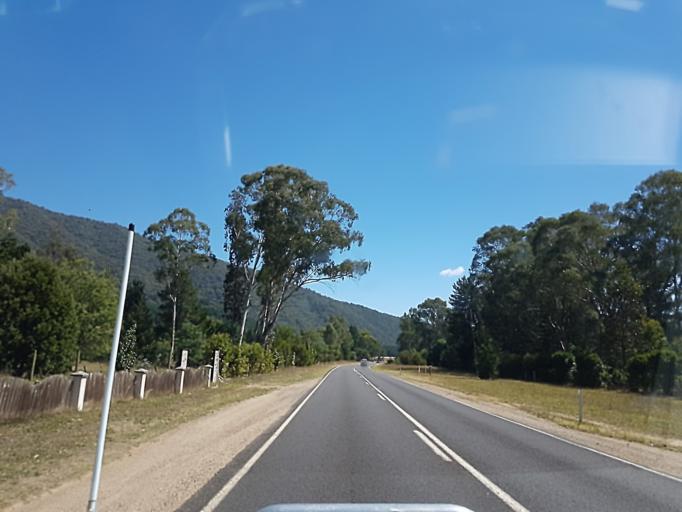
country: AU
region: Victoria
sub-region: Alpine
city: Mount Beauty
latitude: -36.7693
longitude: 147.0268
